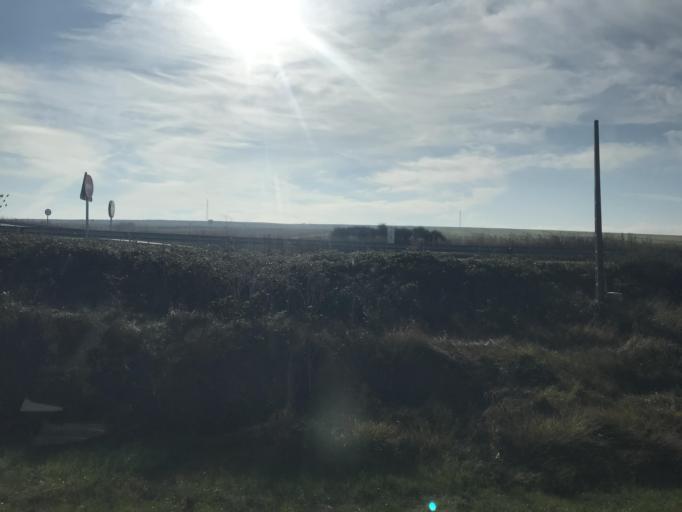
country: ES
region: Castille and Leon
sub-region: Provincia de Burgos
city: Berzosa de Bureba
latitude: 42.6169
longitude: -3.2594
